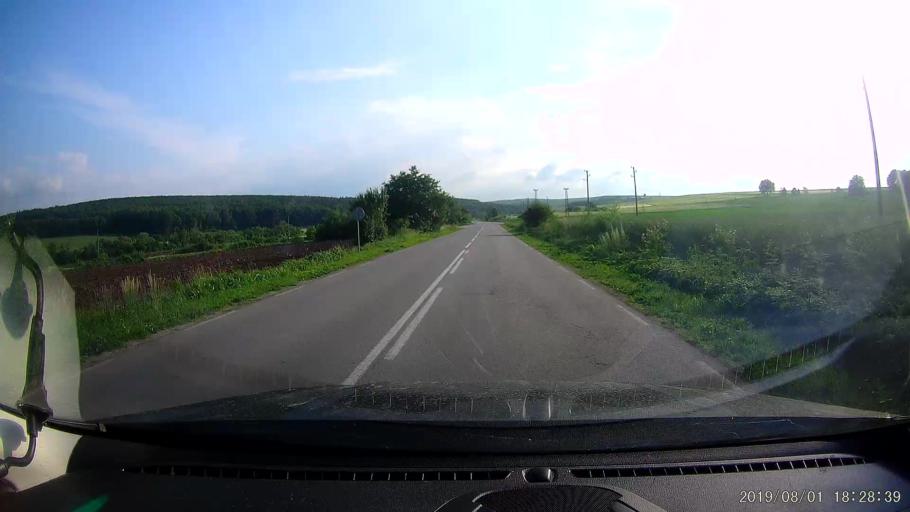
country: BG
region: Shumen
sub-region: Obshtina Venets
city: Venets
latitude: 43.5722
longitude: 26.9604
